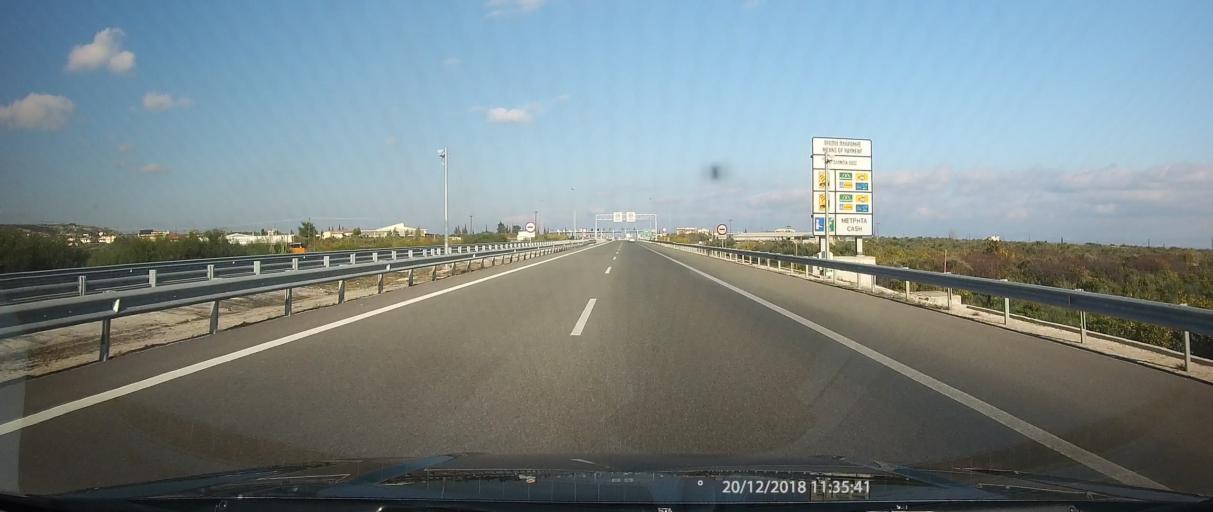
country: GR
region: Peloponnese
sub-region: Nomos Korinthias
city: Moulki
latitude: 37.9908
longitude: 22.7359
